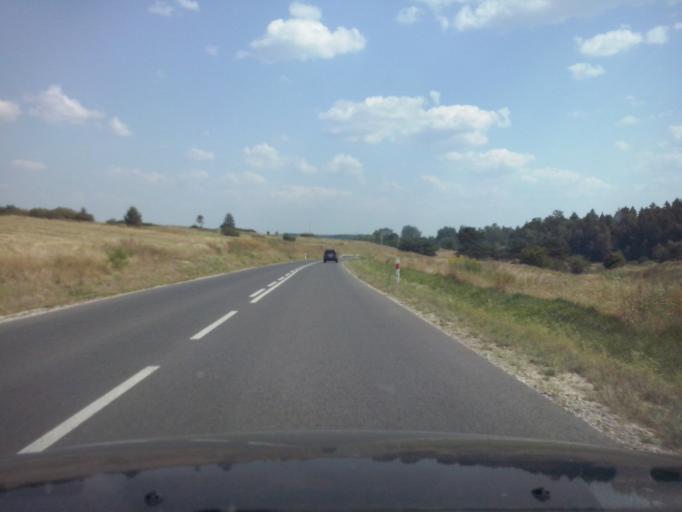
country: PL
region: Swietokrzyskie
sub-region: Powiat staszowski
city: Staszow
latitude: 50.5850
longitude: 21.0982
